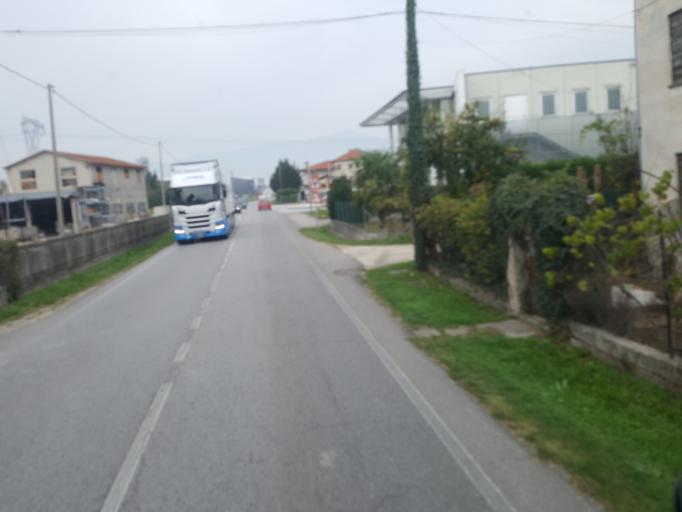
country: IT
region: Veneto
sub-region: Provincia di Treviso
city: Ramon
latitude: 45.7042
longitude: 11.8722
